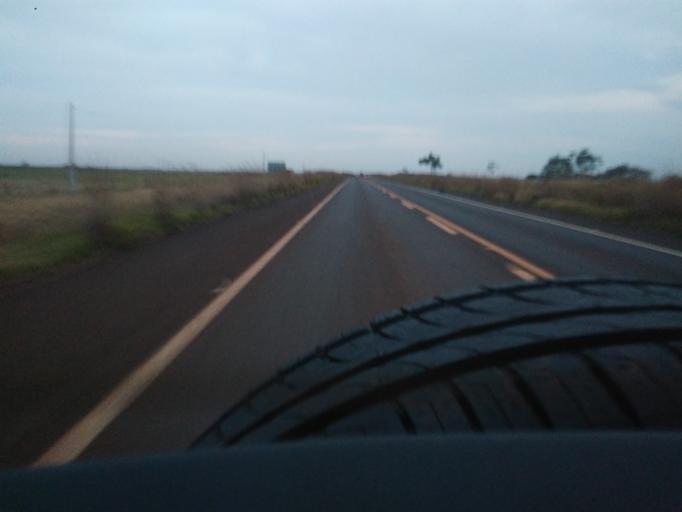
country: BR
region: Mato Grosso do Sul
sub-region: Ponta Pora
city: Ponta Pora
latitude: -22.5472
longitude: -55.4797
